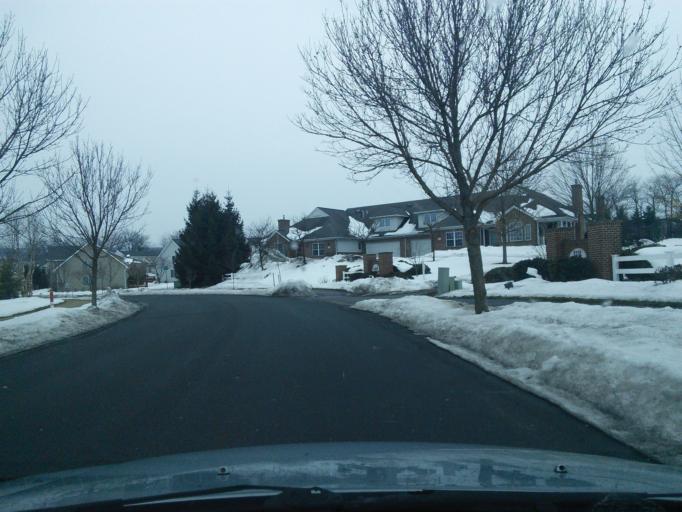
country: US
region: Pennsylvania
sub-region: Centre County
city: State College
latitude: 40.7695
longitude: -77.8702
